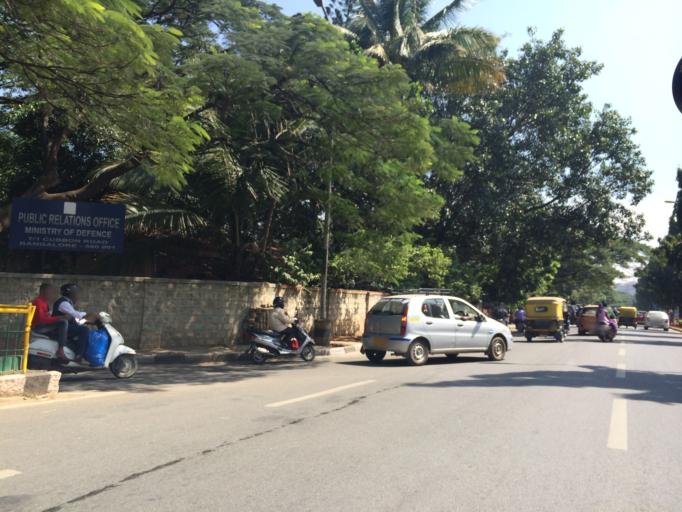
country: IN
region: Karnataka
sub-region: Bangalore Urban
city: Bangalore
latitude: 12.9780
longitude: 77.6066
